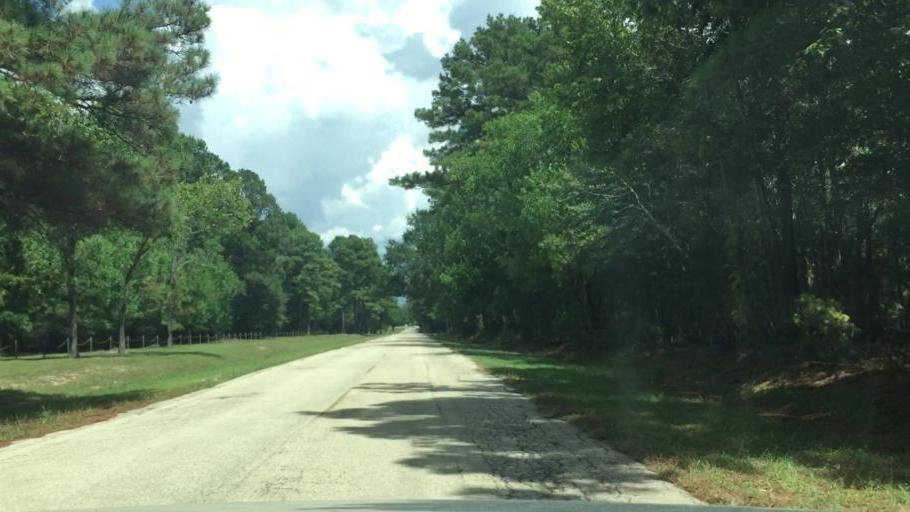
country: US
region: Texas
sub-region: Harris County
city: Jersey Village
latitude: 29.8133
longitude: -95.6246
